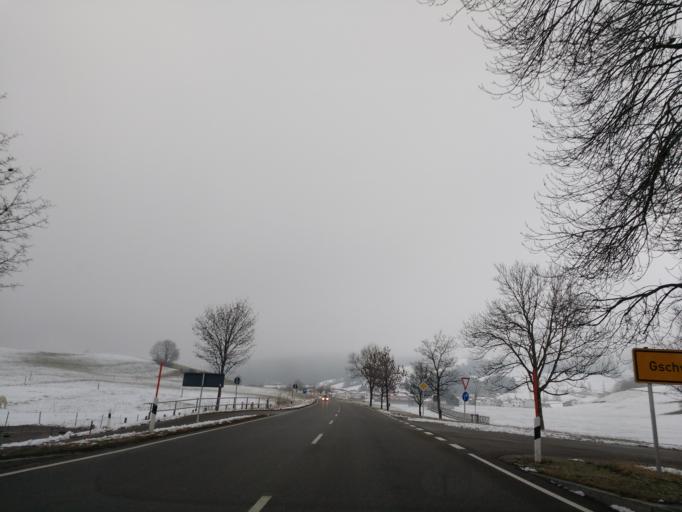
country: DE
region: Bavaria
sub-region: Swabia
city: Nesselwang
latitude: 47.6274
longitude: 10.4861
